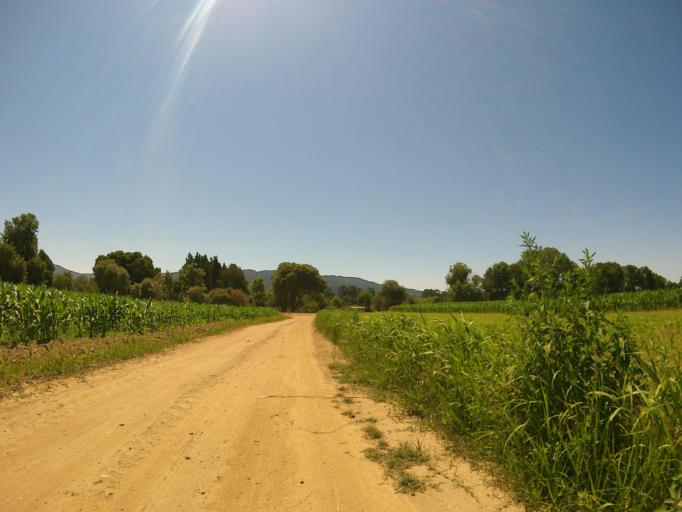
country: PT
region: Viana do Castelo
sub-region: Viana do Castelo
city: Darque
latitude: 41.7187
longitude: -8.7046
